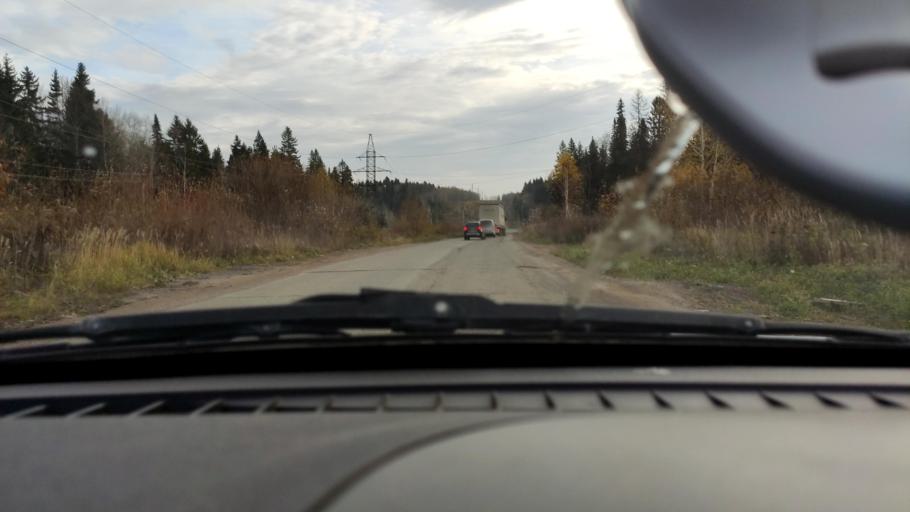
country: RU
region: Perm
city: Perm
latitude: 58.0888
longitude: 56.4226
